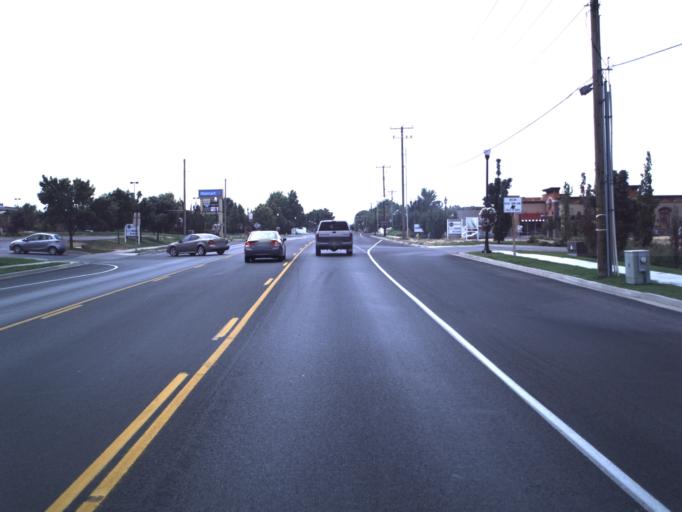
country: US
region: Utah
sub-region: Davis County
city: Clinton
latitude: 41.1391
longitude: -112.0645
